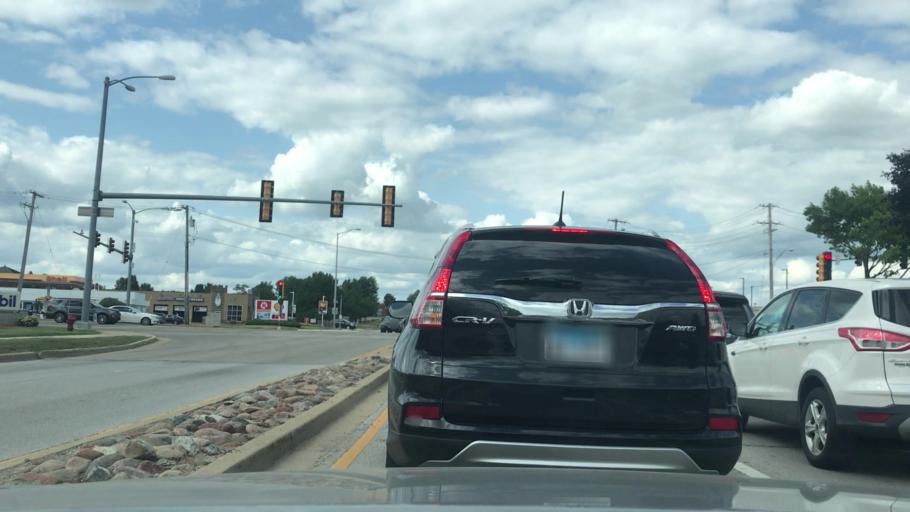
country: US
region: Illinois
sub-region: Kane County
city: Aurora
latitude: 41.7587
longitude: -88.2431
